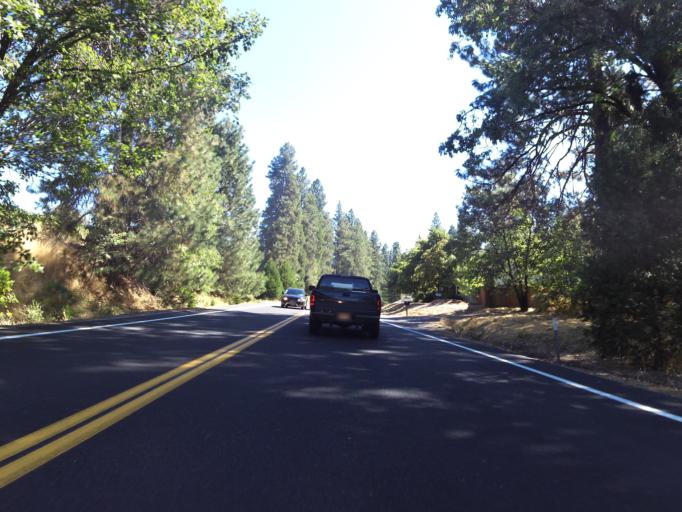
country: US
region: California
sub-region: Calaveras County
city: Forest Meadows
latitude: 38.1704
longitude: -120.4106
